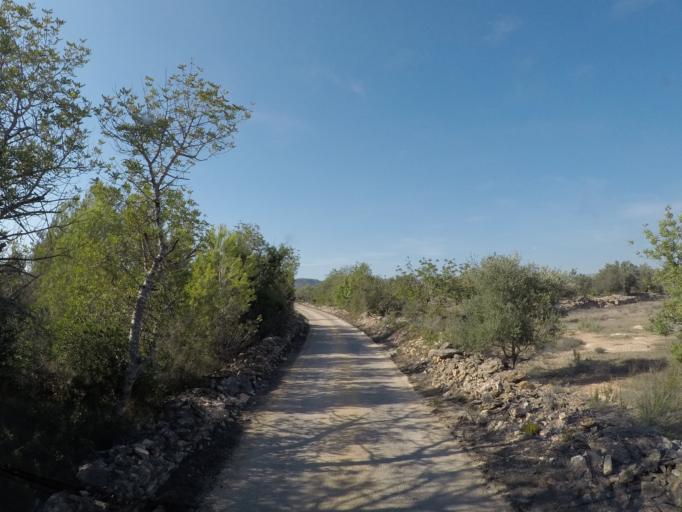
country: ES
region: Catalonia
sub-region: Provincia de Tarragona
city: El Perello
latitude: 40.9007
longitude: 0.7308
